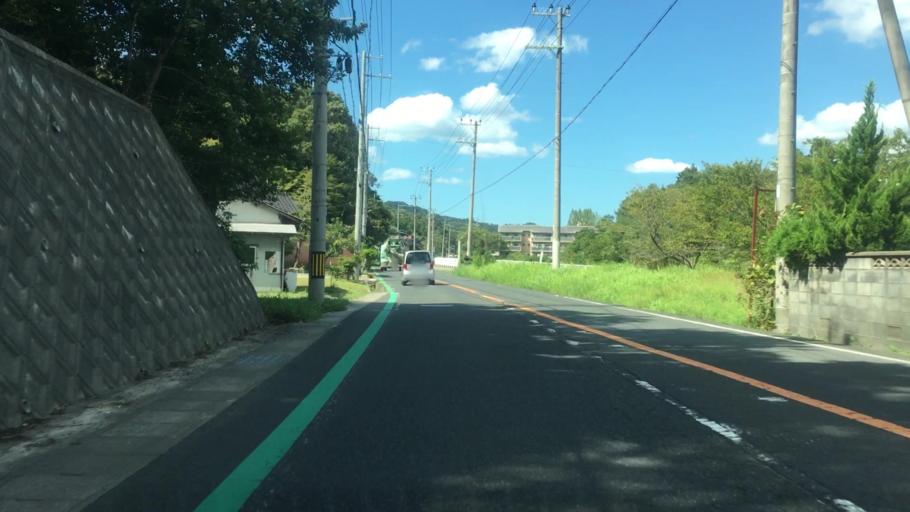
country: JP
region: Kyoto
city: Miyazu
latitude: 35.6132
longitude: 135.0542
